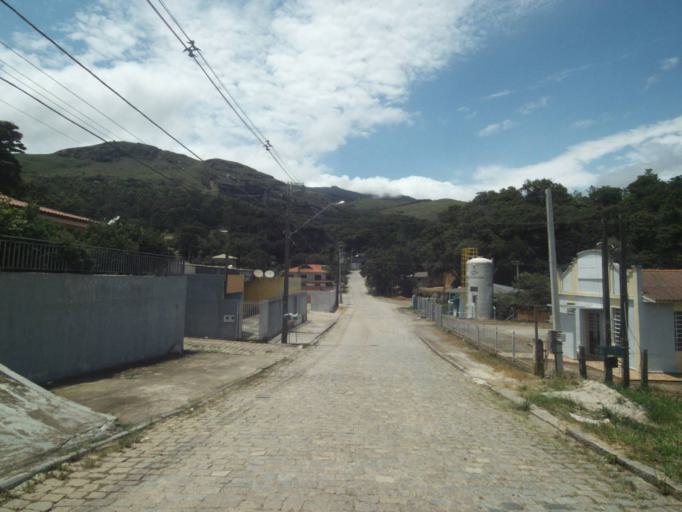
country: BR
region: Parana
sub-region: Campina Grande Do Sul
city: Campina Grande do Sul
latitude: -25.1091
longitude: -48.8357
